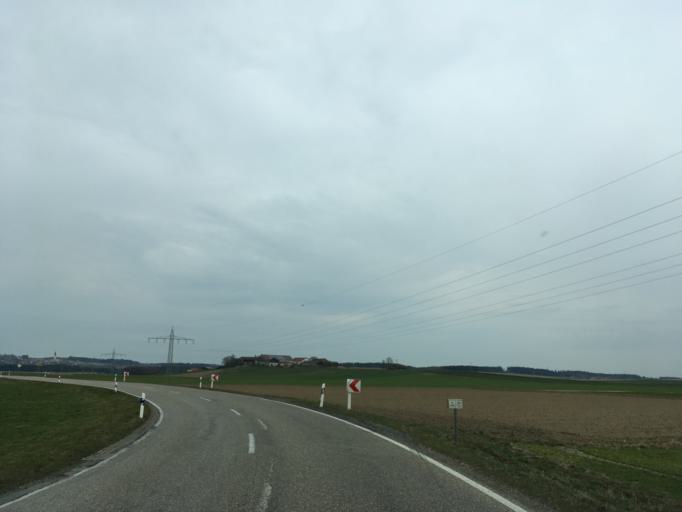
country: DE
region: Bavaria
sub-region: Upper Bavaria
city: Schnaitsee
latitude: 48.0362
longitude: 12.3723
